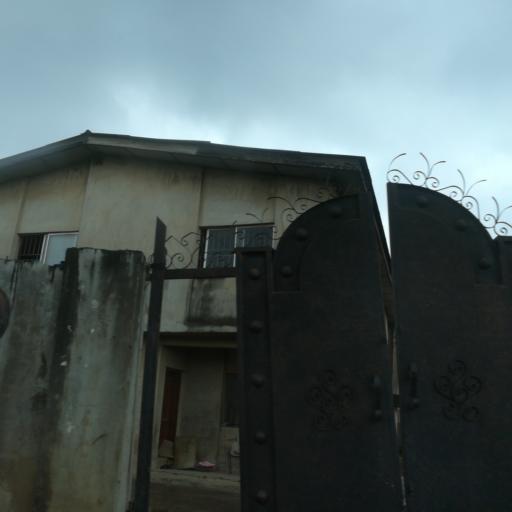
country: NG
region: Lagos
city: Agege
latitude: 6.5941
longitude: 3.2970
